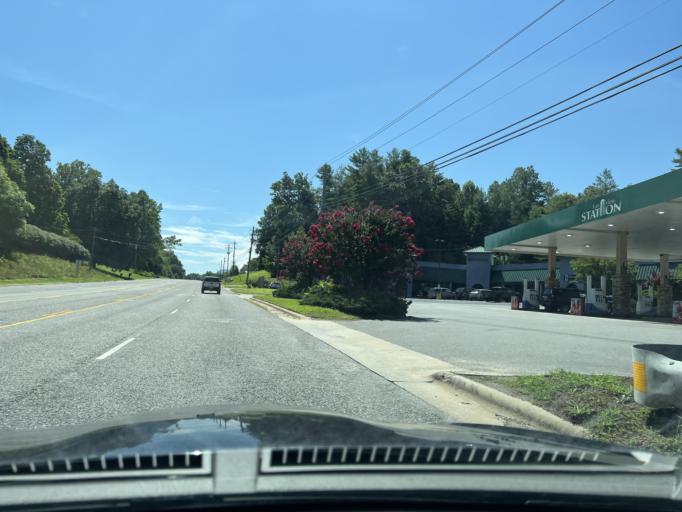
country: US
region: North Carolina
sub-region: Buncombe County
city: Fairview
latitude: 35.5258
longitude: -82.4247
